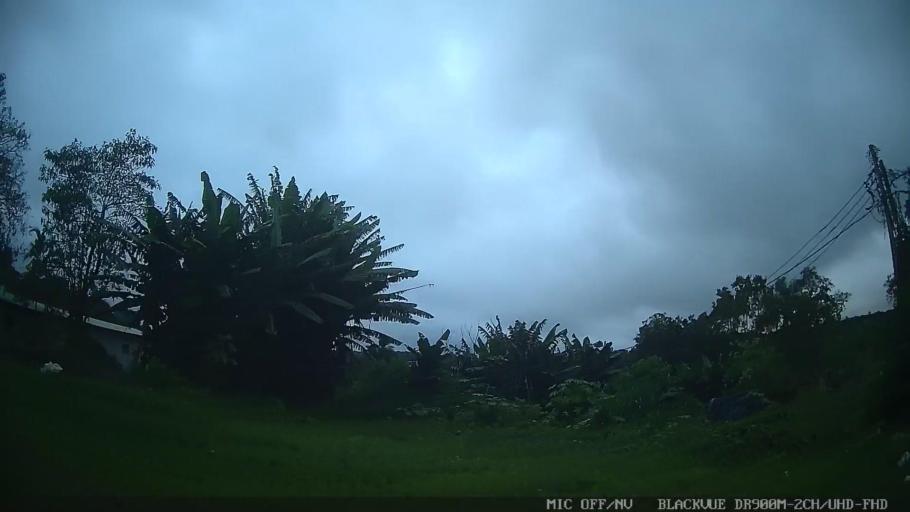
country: BR
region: Sao Paulo
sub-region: Biritiba-Mirim
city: Biritiba Mirim
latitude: -23.5416
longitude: -46.0924
